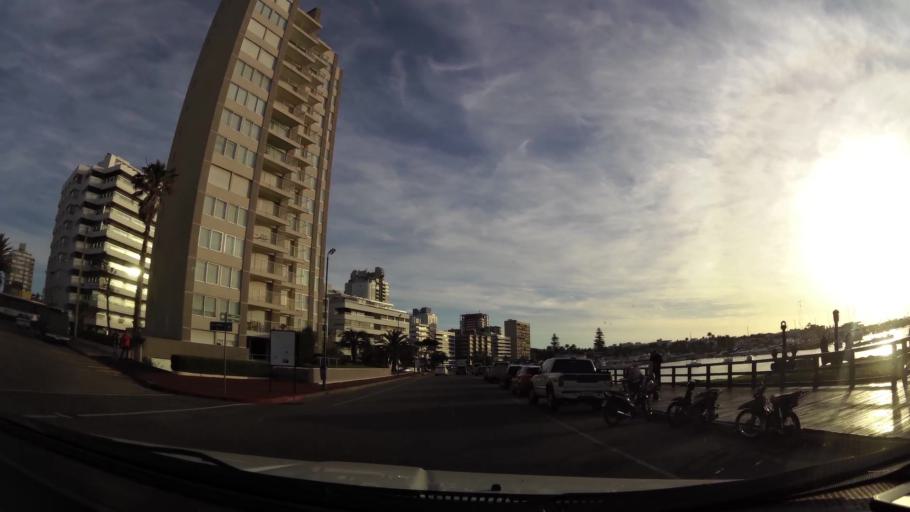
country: UY
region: Maldonado
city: Punta del Este
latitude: -34.9622
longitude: -54.9461
